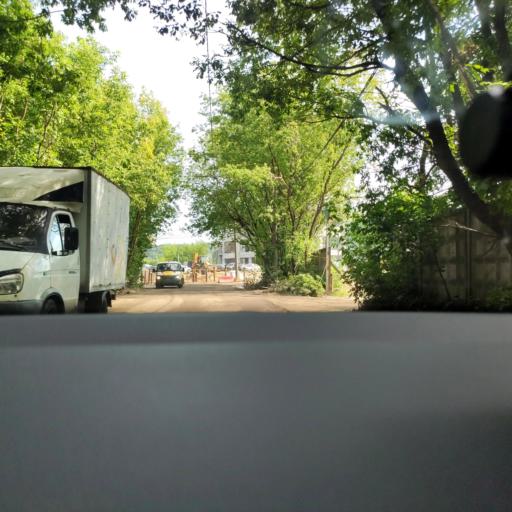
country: RU
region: Moskovskaya
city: Fili
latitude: 55.7475
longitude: 37.4527
